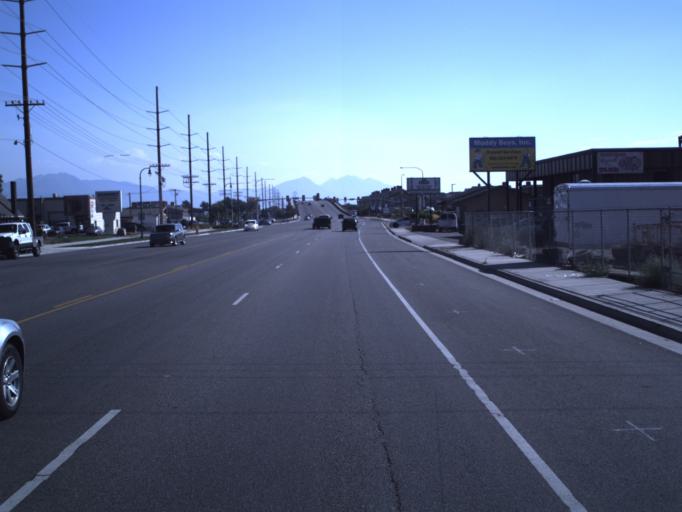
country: US
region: Utah
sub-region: Utah County
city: Orem
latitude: 40.2993
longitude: -111.7340
